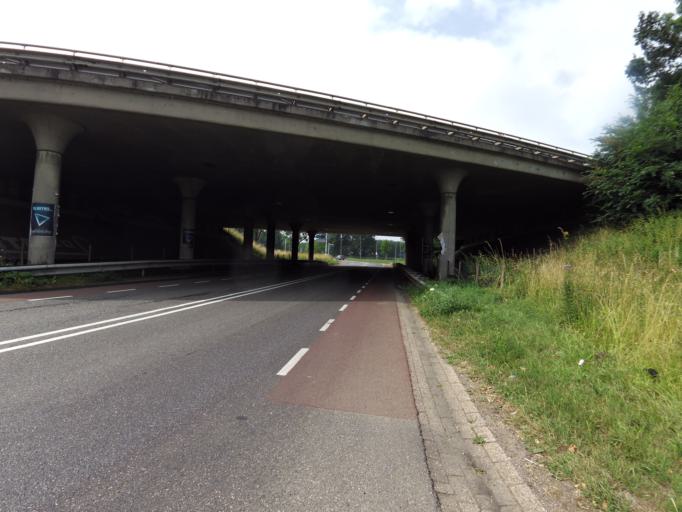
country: NL
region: Limburg
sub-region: Gemeente Voerendaal
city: Klimmen
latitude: 50.8804
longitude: 5.9038
